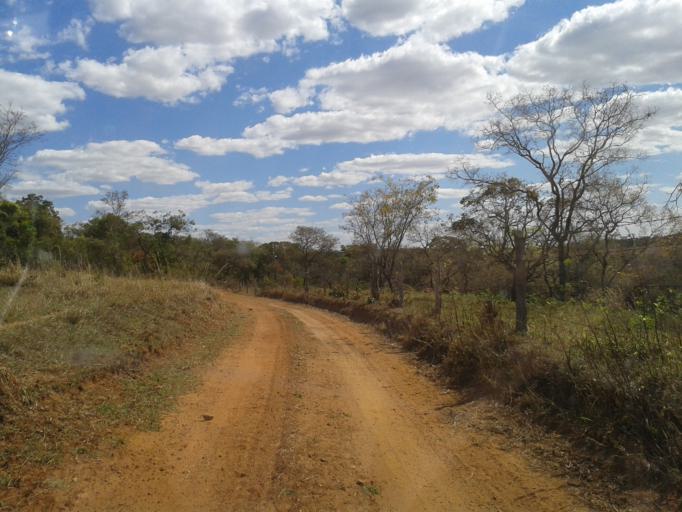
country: BR
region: Minas Gerais
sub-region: Monte Alegre De Minas
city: Monte Alegre de Minas
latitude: -18.7948
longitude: -49.0890
